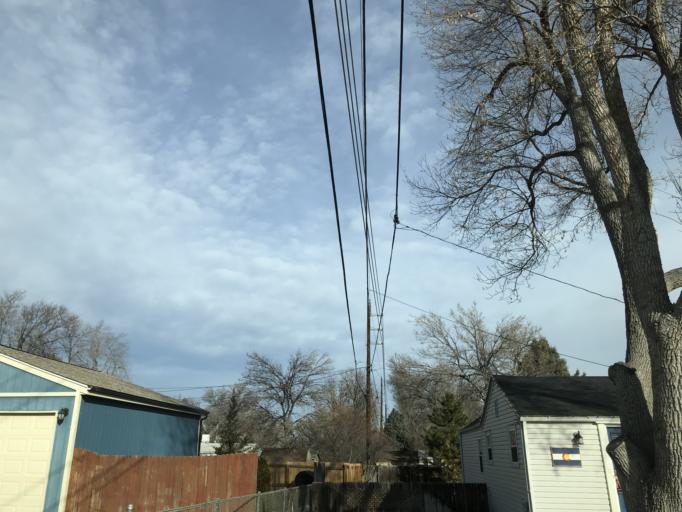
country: US
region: Colorado
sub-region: Arapahoe County
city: Littleton
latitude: 39.6006
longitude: -105.0087
